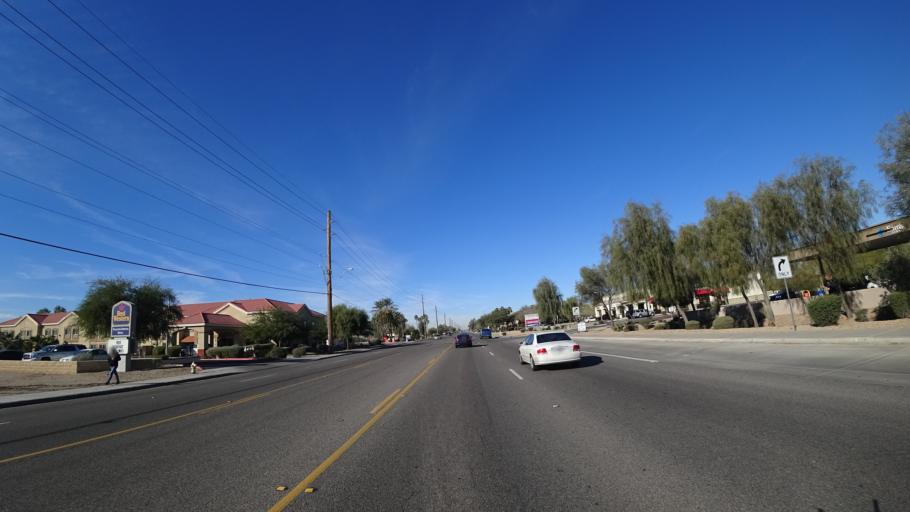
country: US
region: Arizona
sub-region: Maricopa County
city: Tolleson
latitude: 33.4653
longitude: -112.2406
